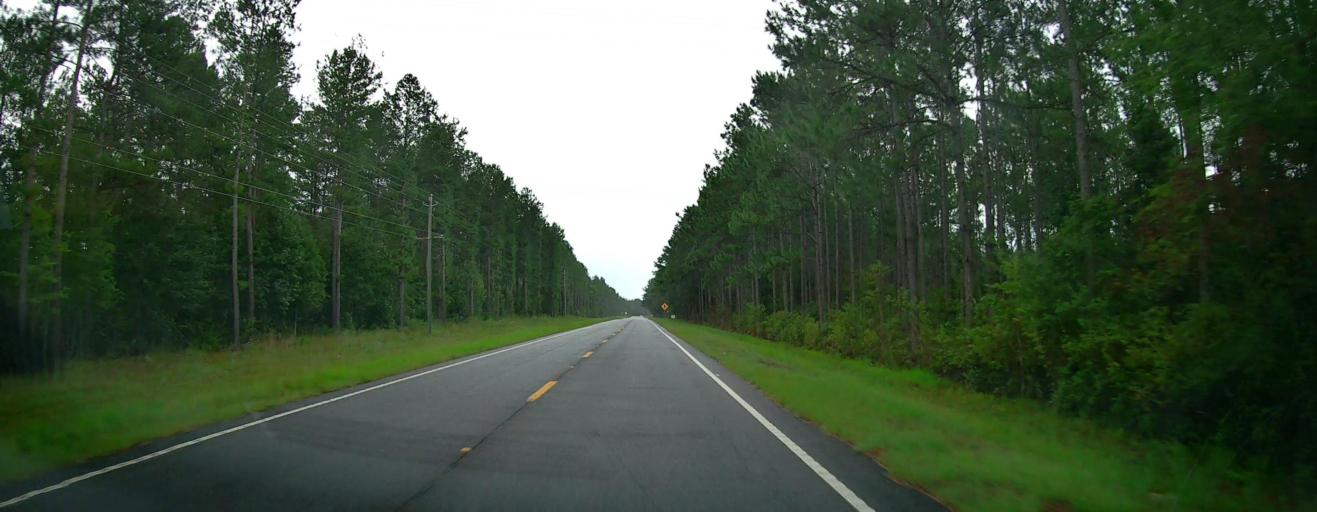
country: US
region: Georgia
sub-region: Ware County
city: Deenwood
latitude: 31.2761
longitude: -82.5335
